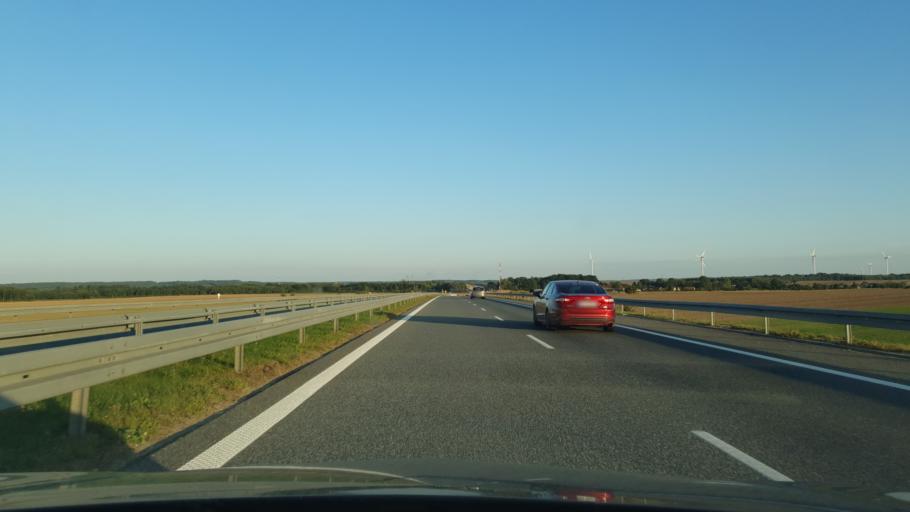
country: PL
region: Pomeranian Voivodeship
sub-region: Powiat slupski
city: Kobylnica
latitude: 54.4374
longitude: 16.9563
